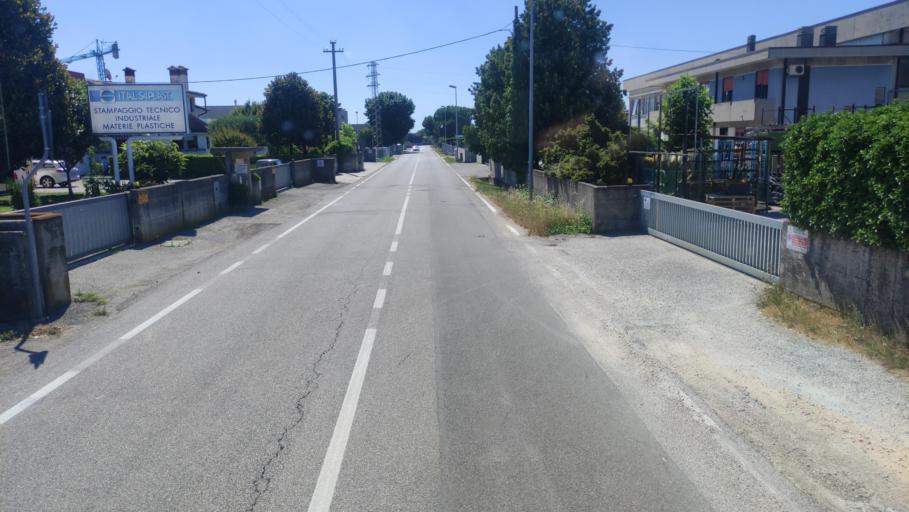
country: IT
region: Veneto
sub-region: Provincia di Treviso
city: Musano
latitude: 45.7399
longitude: 12.1183
